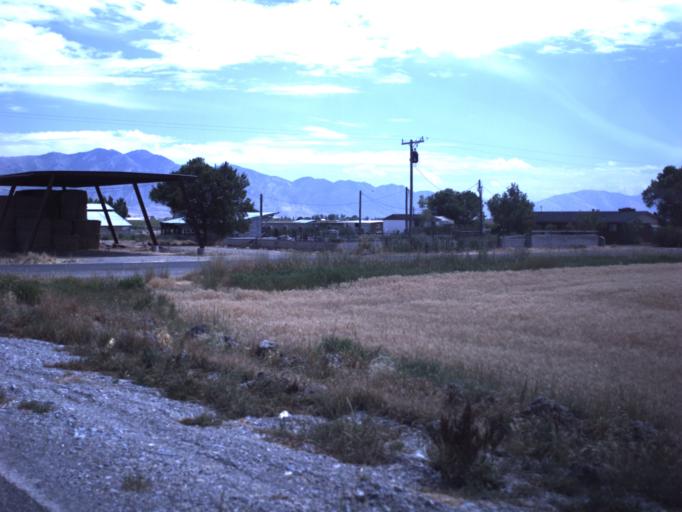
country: US
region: Utah
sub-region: Box Elder County
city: Tremonton
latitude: 41.7100
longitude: -112.2394
